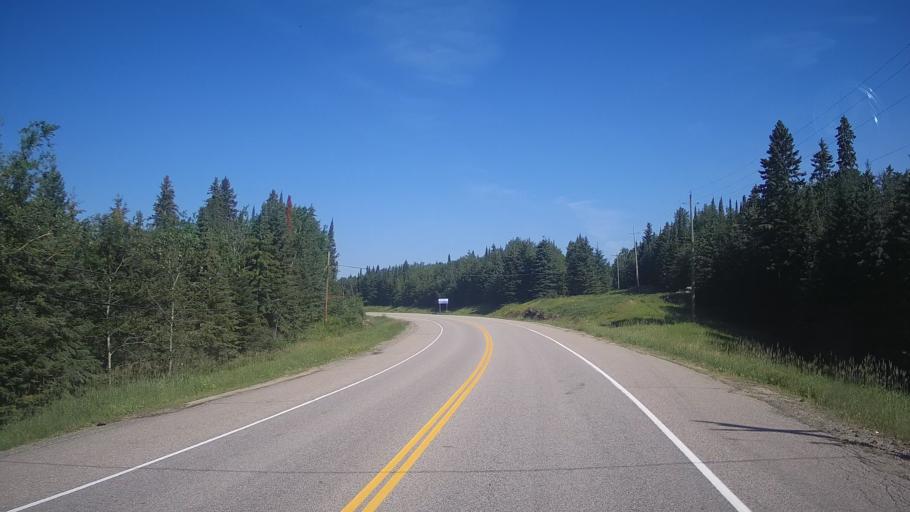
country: CA
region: Ontario
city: Dryden
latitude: 49.7827
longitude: -92.6997
